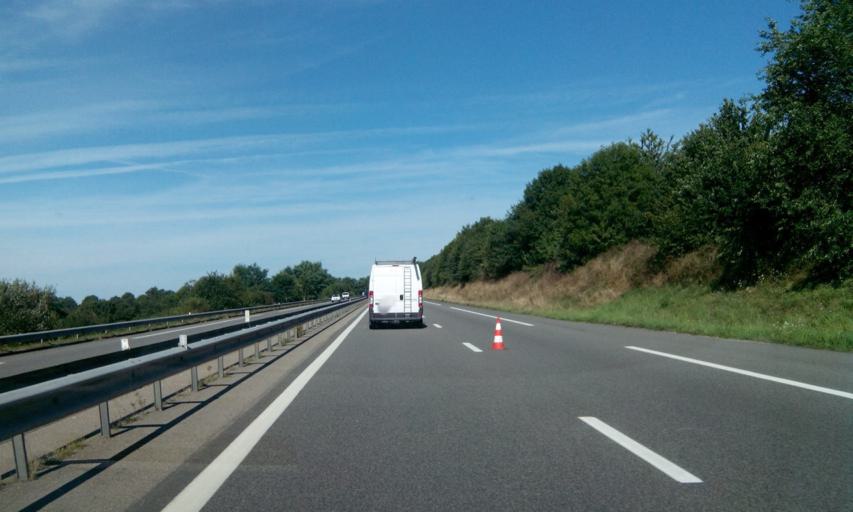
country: FR
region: Limousin
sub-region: Departement de la Haute-Vienne
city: Saint-Victurnien
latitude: 45.8910
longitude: 1.0466
